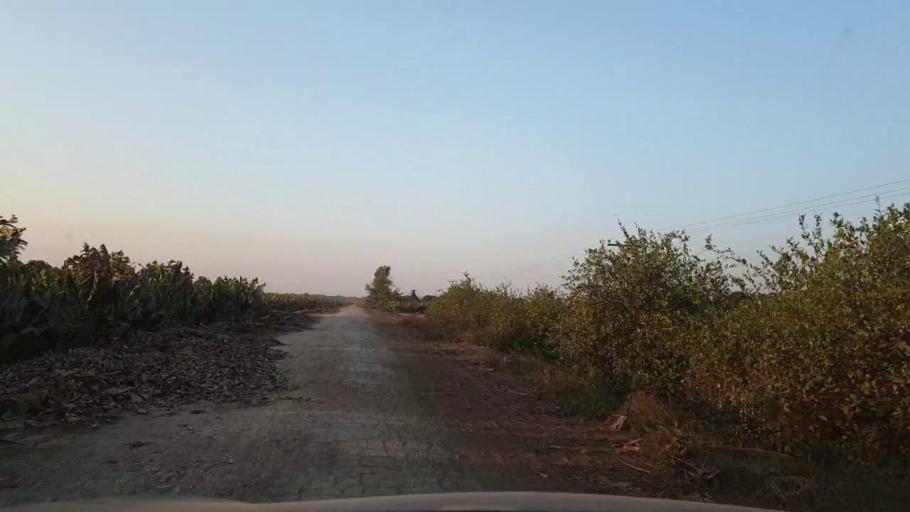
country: PK
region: Sindh
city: Tando Allahyar
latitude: 25.5200
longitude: 68.7373
